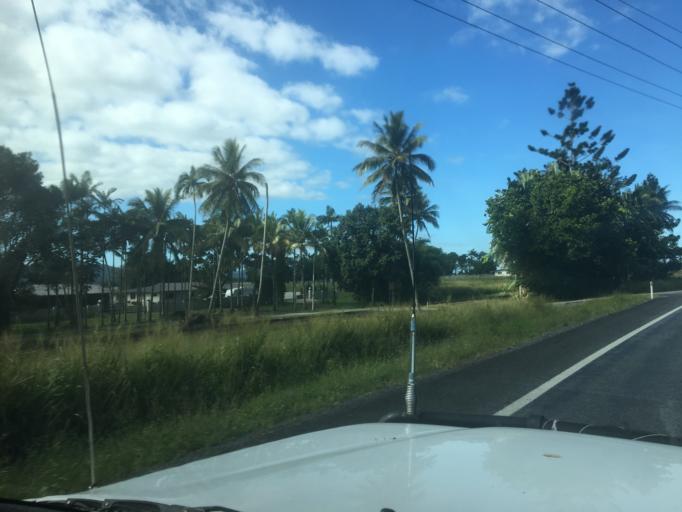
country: AU
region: Queensland
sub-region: Cassowary Coast
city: Innisfail
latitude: -17.2971
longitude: 145.9282
